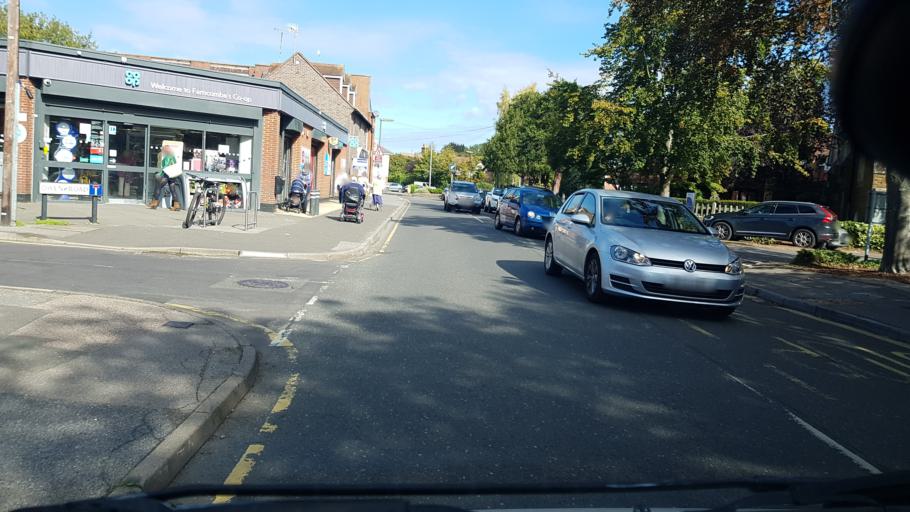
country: GB
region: England
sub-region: Surrey
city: Godalming
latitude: 51.1954
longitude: -0.6041
